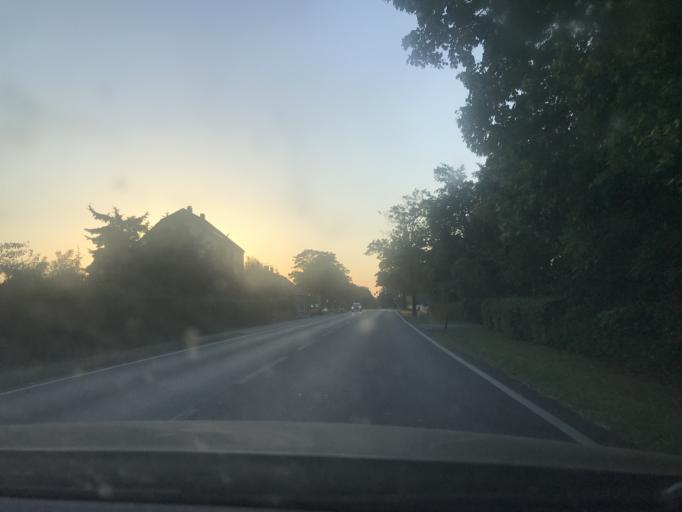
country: DE
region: North Rhine-Westphalia
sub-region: Regierungsbezirk Dusseldorf
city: Moers
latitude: 51.5017
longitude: 6.6240
